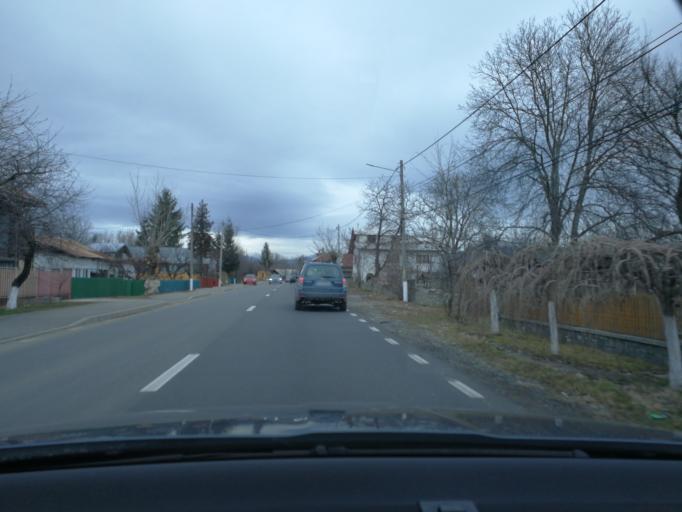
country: RO
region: Prahova
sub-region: Oras Breaza
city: Breaza de Jos
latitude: 45.1651
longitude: 25.6830
